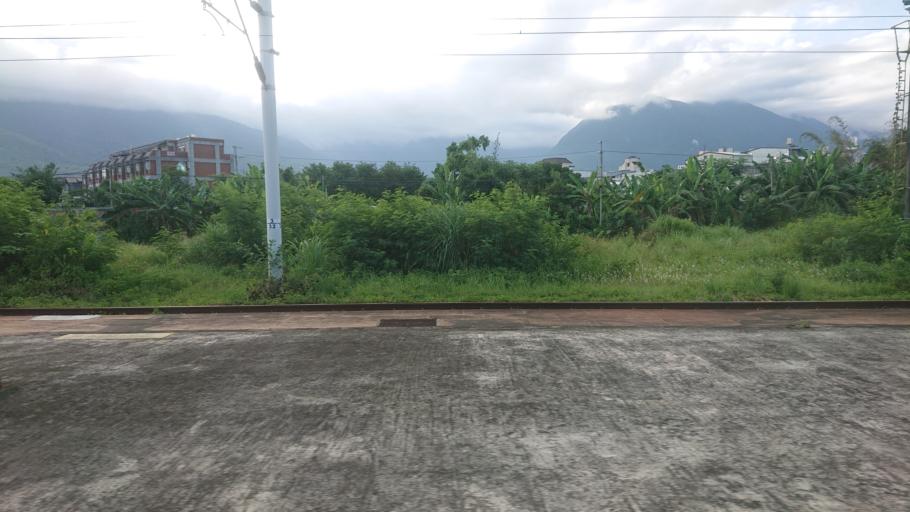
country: TW
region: Taiwan
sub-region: Hualien
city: Hualian
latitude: 23.9666
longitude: 121.5809
